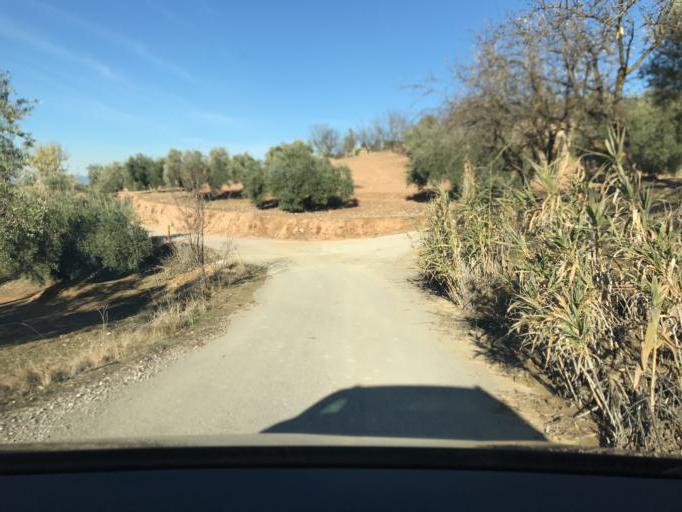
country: ES
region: Andalusia
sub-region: Provincia de Granada
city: Peligros
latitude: 37.2462
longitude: -3.6304
